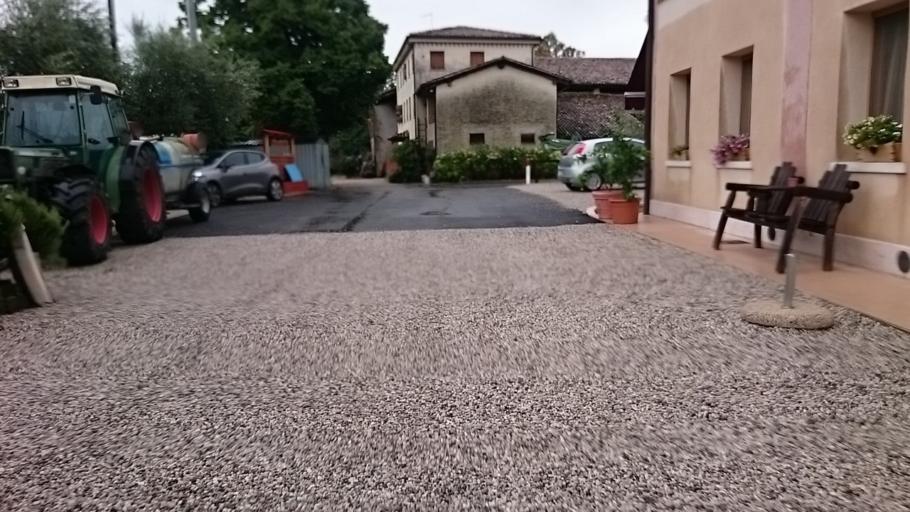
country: IT
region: Veneto
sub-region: Provincia di Treviso
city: Monfumo
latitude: 45.8196
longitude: 11.9155
